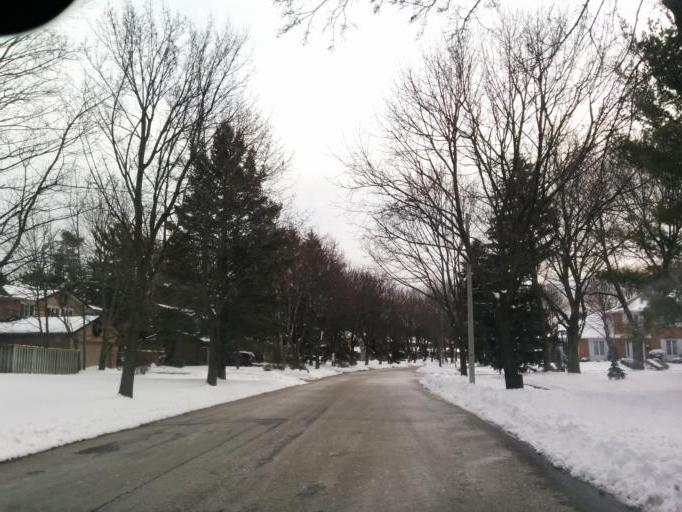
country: CA
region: Ontario
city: Mississauga
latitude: 43.5392
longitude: -79.6566
